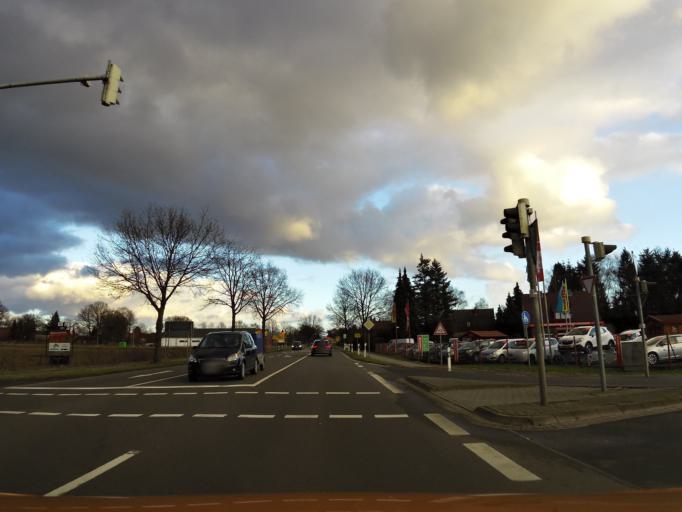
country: DE
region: Lower Saxony
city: Eicklingen
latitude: 52.5483
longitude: 10.1742
